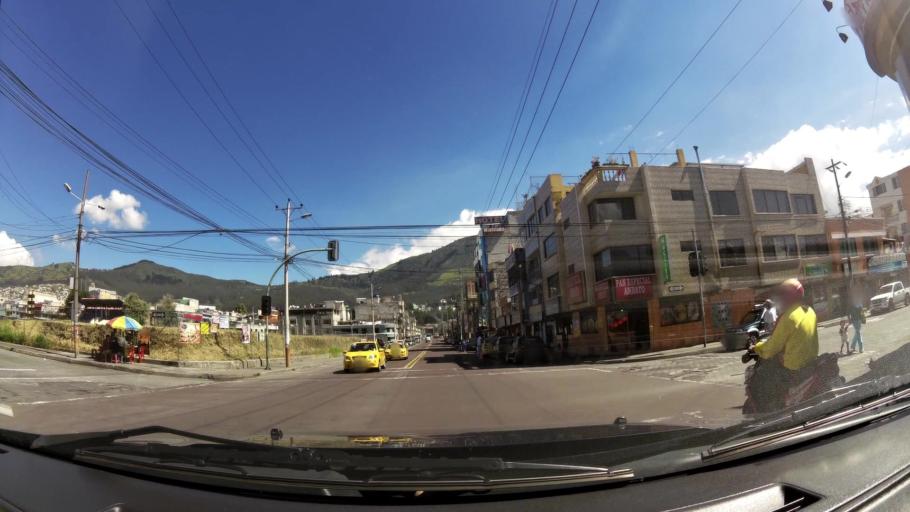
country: EC
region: Pichincha
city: Quito
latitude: -0.2601
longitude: -78.5393
